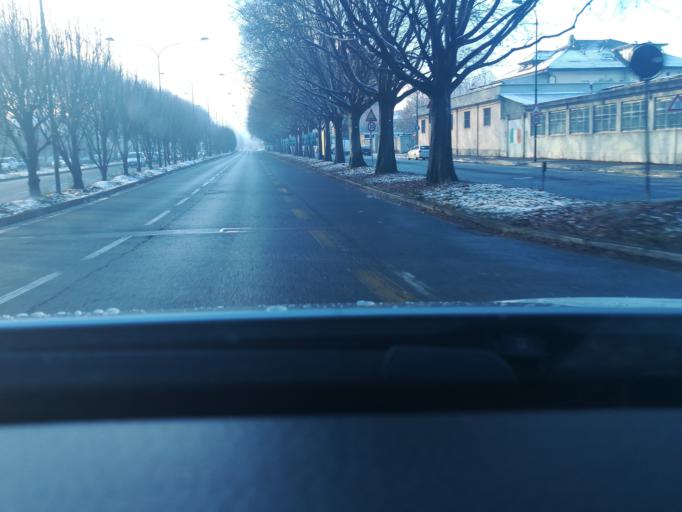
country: IT
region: Piedmont
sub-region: Provincia di Torino
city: Turin
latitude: 45.0904
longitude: 7.6535
